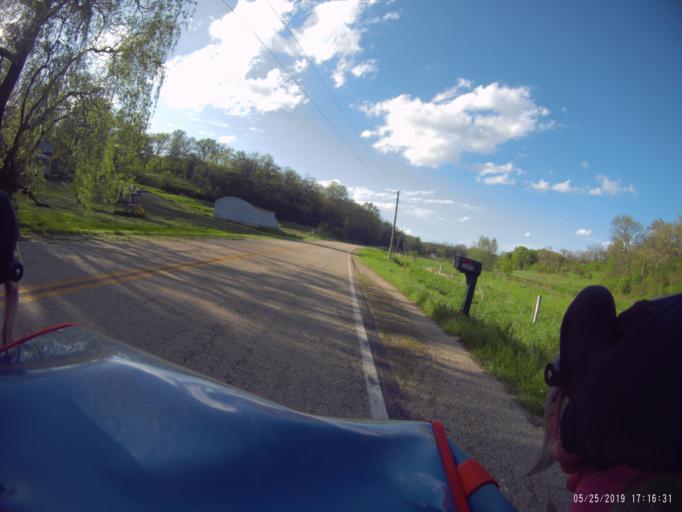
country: US
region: Wisconsin
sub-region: Dane County
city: Mount Horeb
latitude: 42.9701
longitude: -89.7897
